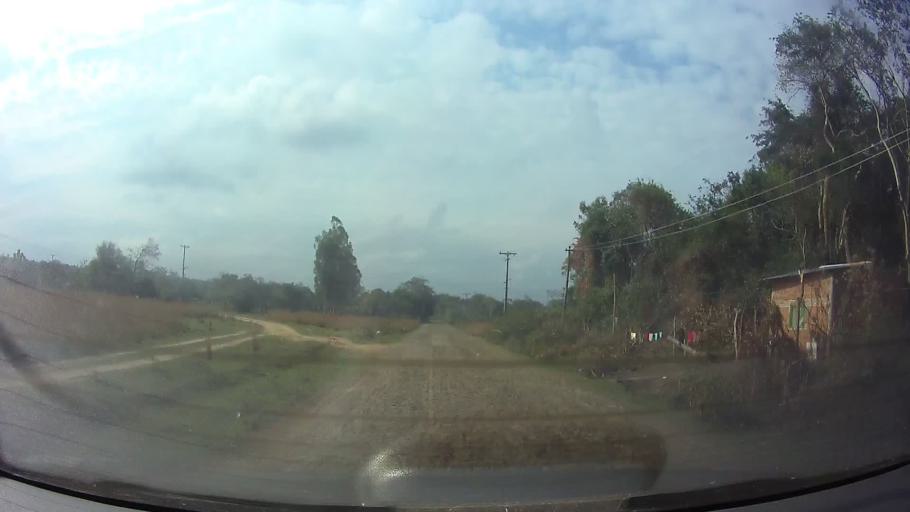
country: PY
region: Cordillera
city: Arroyos y Esteros
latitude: -25.0001
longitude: -57.1953
